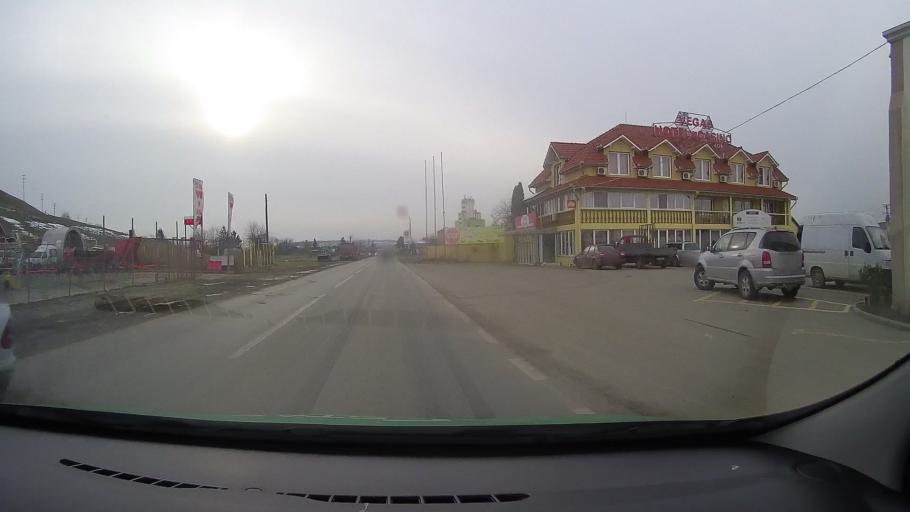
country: RO
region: Hunedoara
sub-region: Municipiul Orastie
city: Orastie
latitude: 45.8619
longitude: 23.2171
